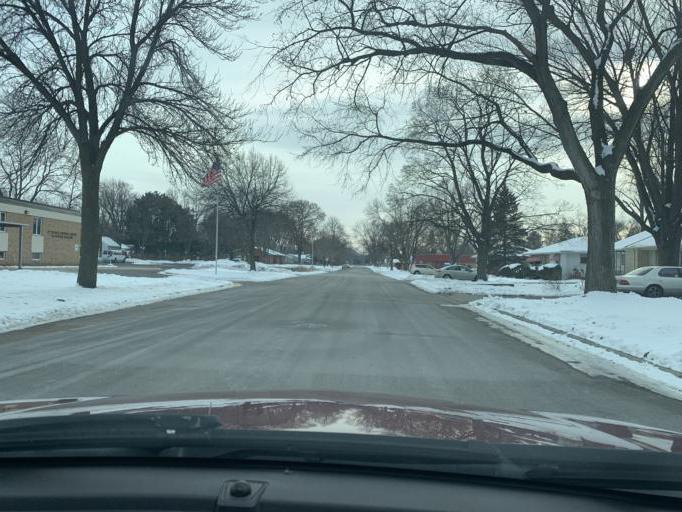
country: US
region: Minnesota
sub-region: Washington County
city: Saint Paul Park
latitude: 44.8415
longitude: -92.9886
